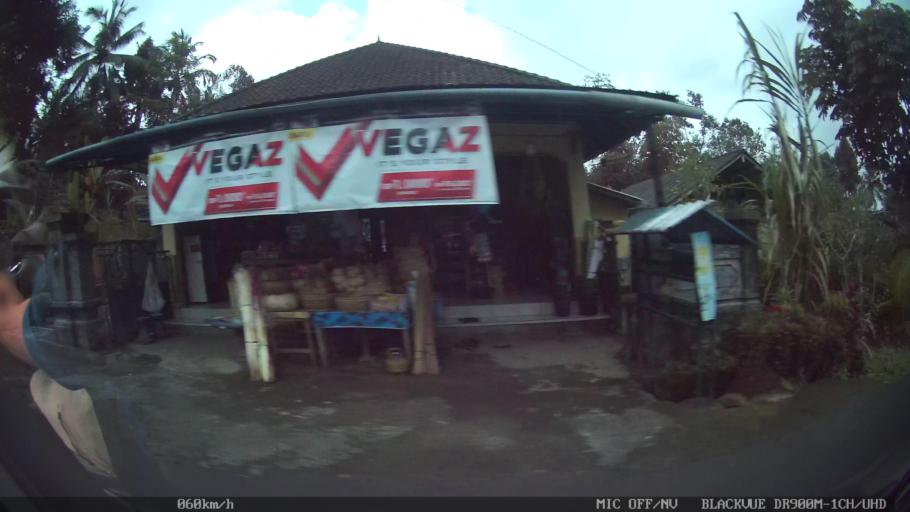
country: ID
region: Bali
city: Banjar Geriana Kangin
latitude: -8.4052
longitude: 115.4400
